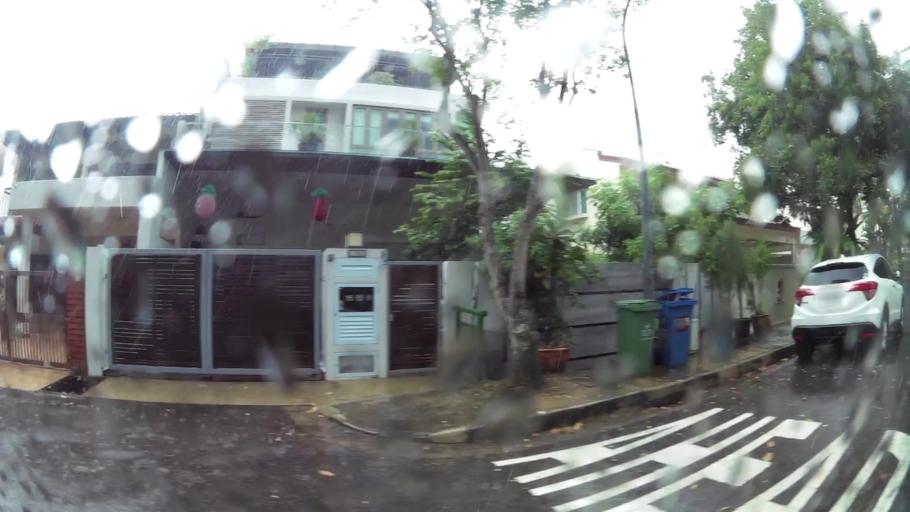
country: SG
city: Singapore
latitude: 1.3391
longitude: 103.9578
